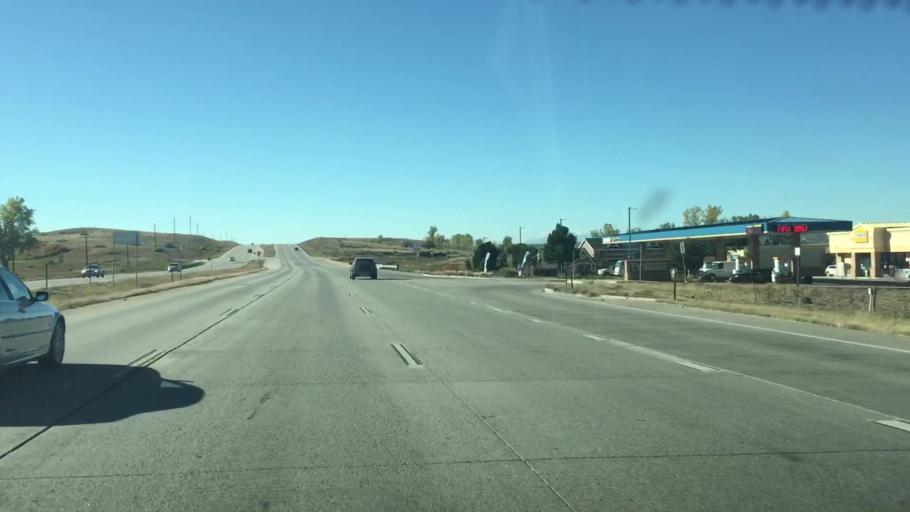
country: US
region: Colorado
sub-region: Douglas County
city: The Pinery
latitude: 39.4770
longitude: -104.7583
